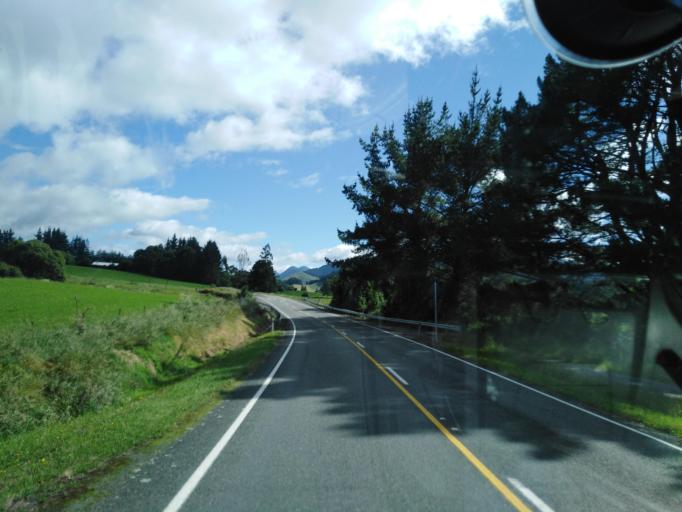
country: NZ
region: Nelson
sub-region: Nelson City
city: Nelson
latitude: -41.2834
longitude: 173.5727
